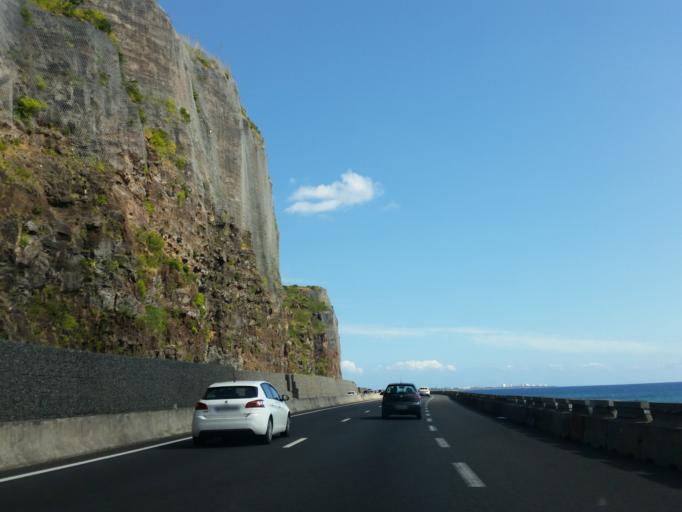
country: RE
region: Reunion
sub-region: Reunion
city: La Possession
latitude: -20.9093
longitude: 55.3578
